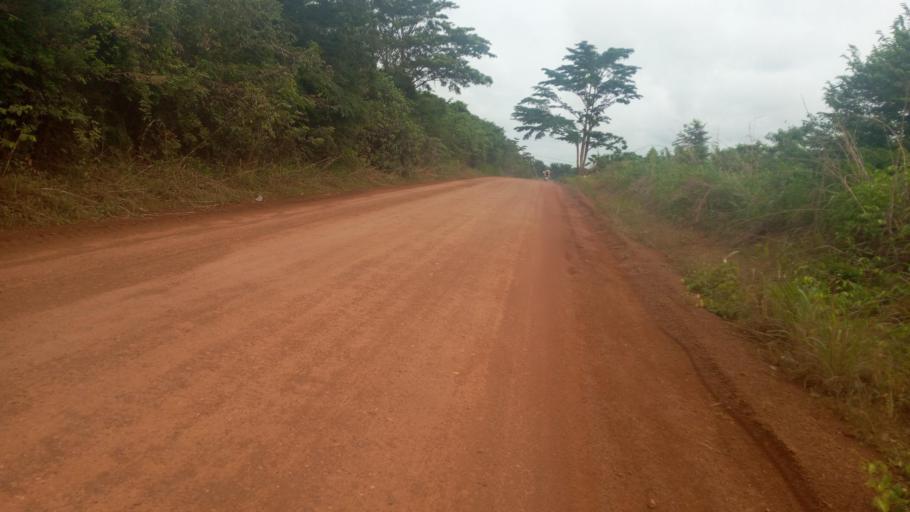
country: SL
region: Southern Province
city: Mogbwemo
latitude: 7.7403
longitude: -12.2866
